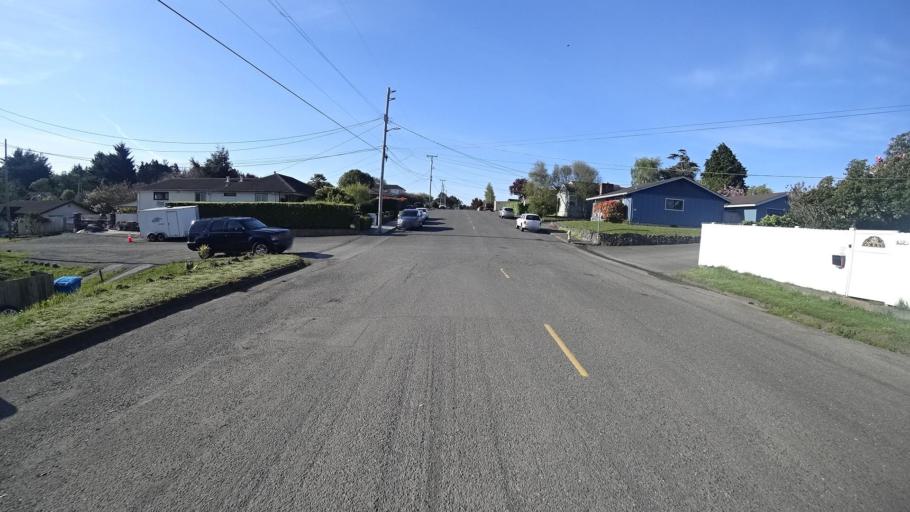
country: US
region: California
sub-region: Humboldt County
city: Bayview
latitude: 40.7680
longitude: -124.1648
